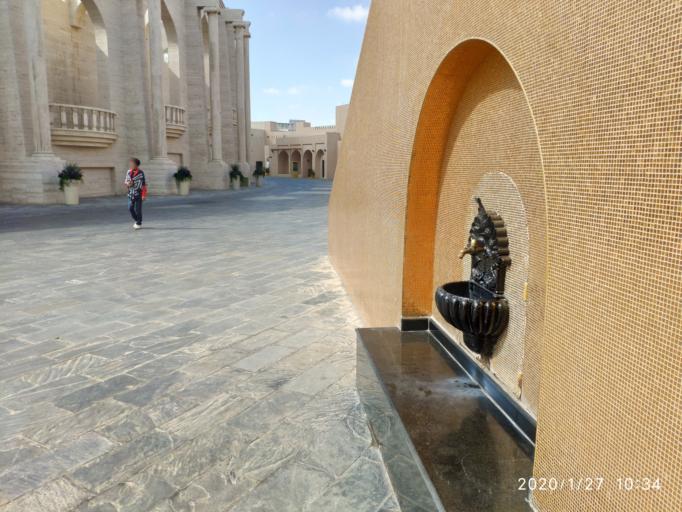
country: QA
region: Baladiyat ad Dawhah
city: Doha
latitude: 25.3608
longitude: 51.5268
